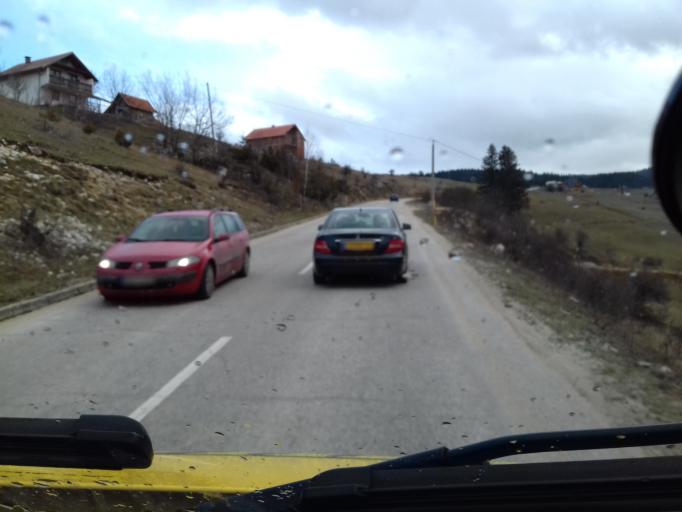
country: BA
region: Federation of Bosnia and Herzegovina
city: Turbe
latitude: 44.3109
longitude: 17.5370
